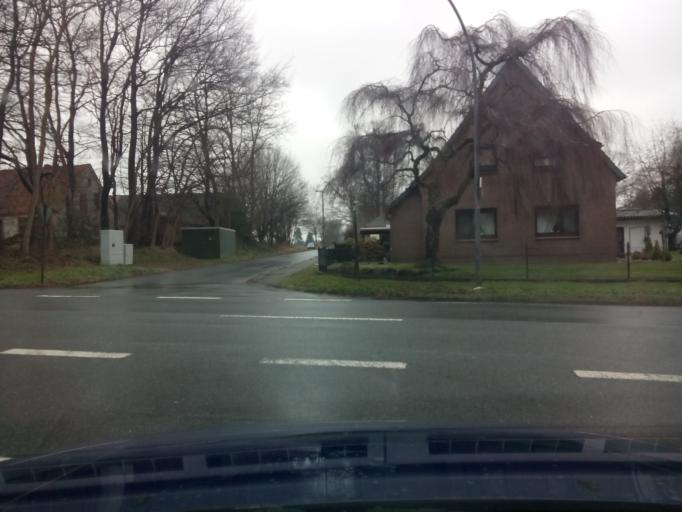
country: DE
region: Lower Saxony
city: Hambergen
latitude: 53.2912
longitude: 8.8167
